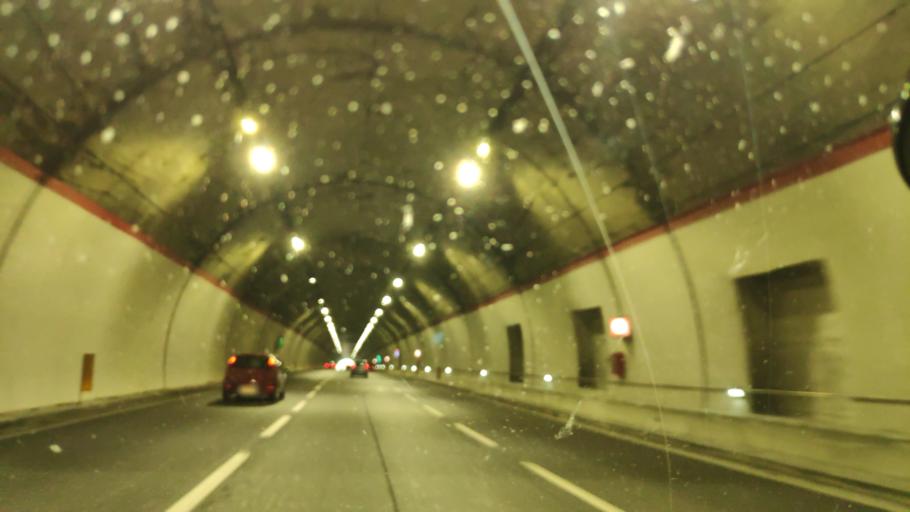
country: IT
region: Campania
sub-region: Provincia di Salerno
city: Pezzano-Filetta
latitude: 40.6750
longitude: 14.8576
